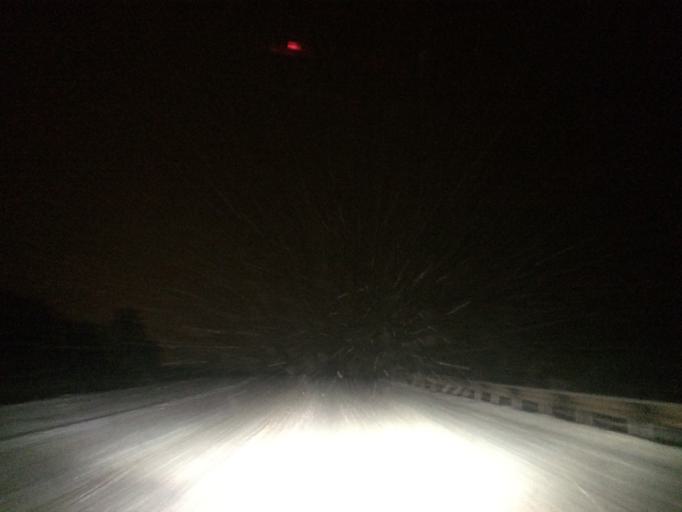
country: RU
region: Tula
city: Dubna
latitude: 54.0958
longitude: 37.0979
